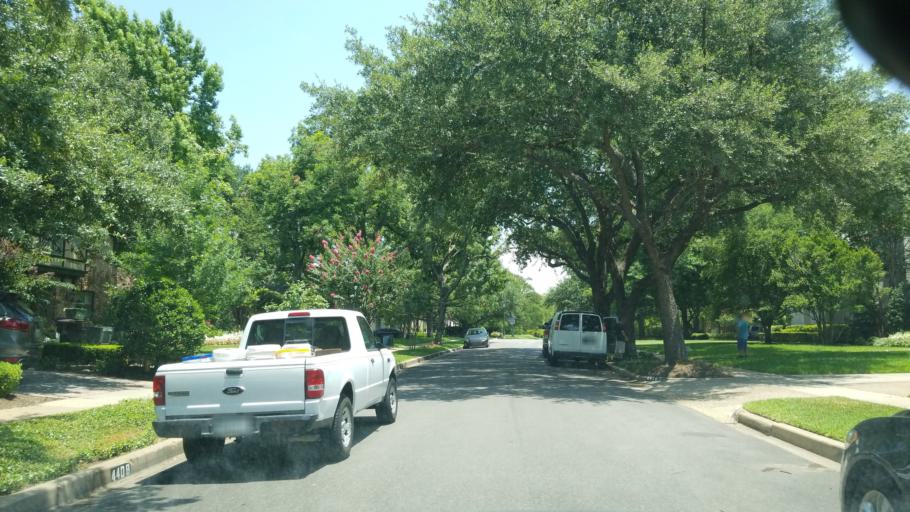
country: US
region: Texas
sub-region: Dallas County
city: Highland Park
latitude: 32.8280
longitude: -96.8105
